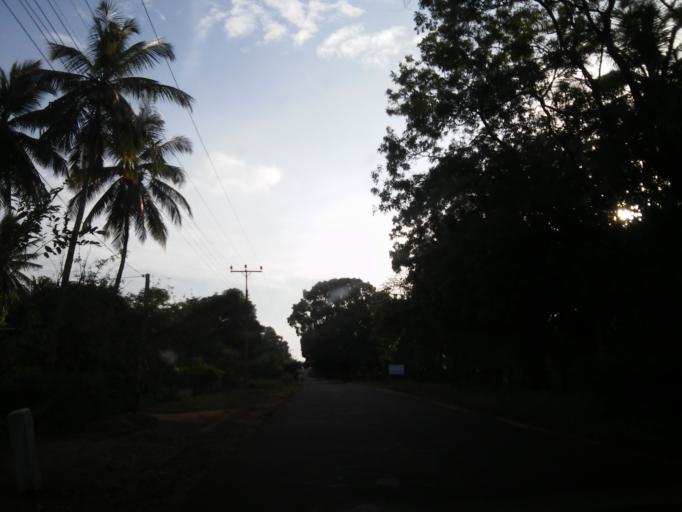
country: LK
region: Central
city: Sigiriya
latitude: 8.1423
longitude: 80.6403
